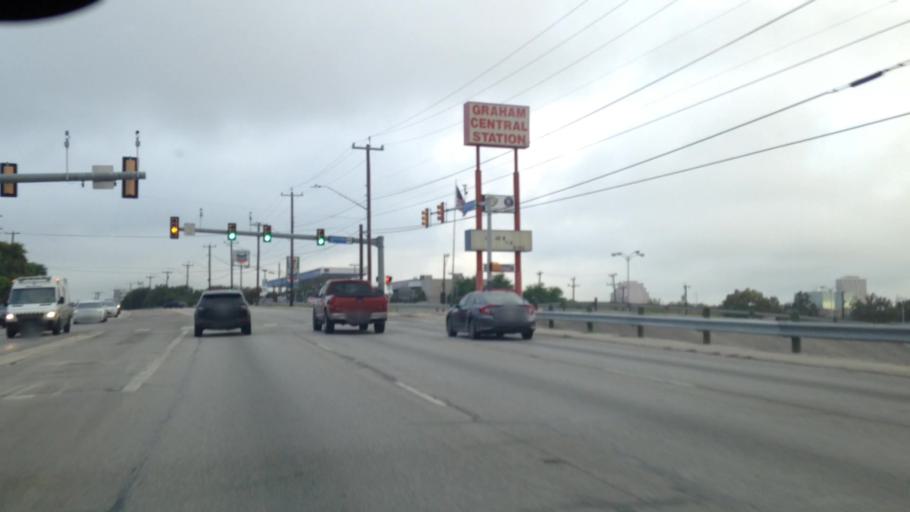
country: US
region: Texas
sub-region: Bexar County
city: Balcones Heights
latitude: 29.4968
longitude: -98.5558
